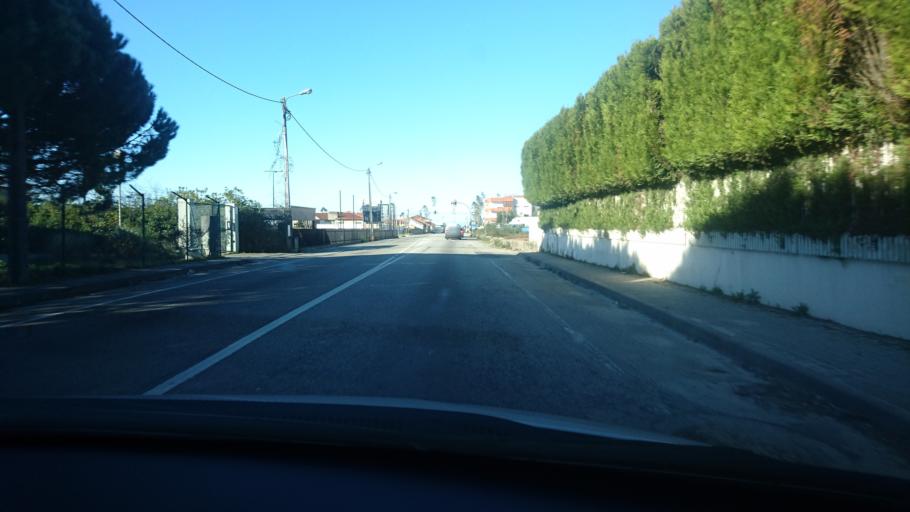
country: PT
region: Aveiro
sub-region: Santa Maria da Feira
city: Sao Joao de Ver
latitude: 40.9517
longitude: -8.5183
